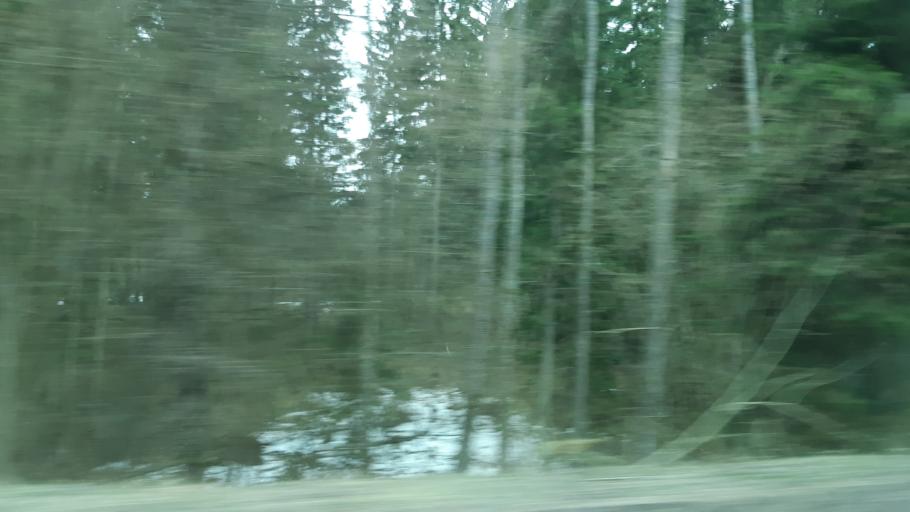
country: PL
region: Podlasie
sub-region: Suwalki
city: Suwalki
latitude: 54.3018
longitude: 22.9574
